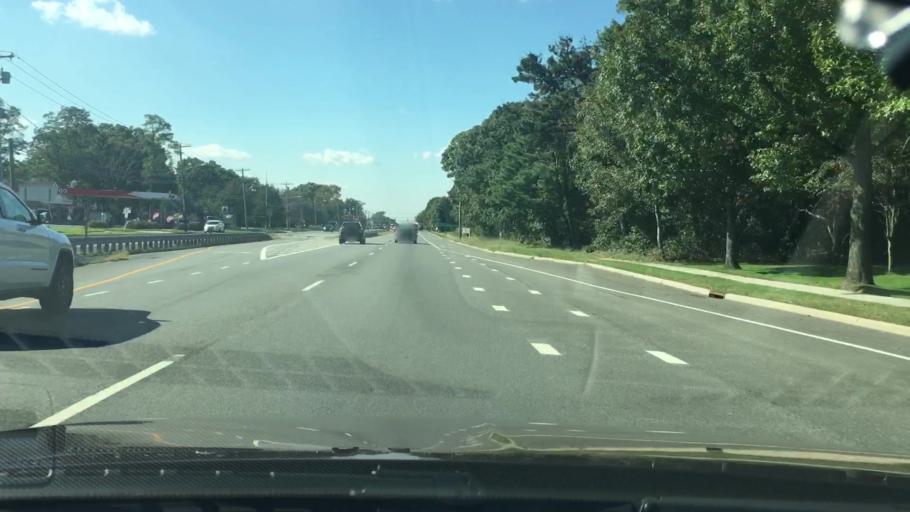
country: US
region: New York
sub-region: Suffolk County
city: Bohemia
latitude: 40.7878
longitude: -73.1325
